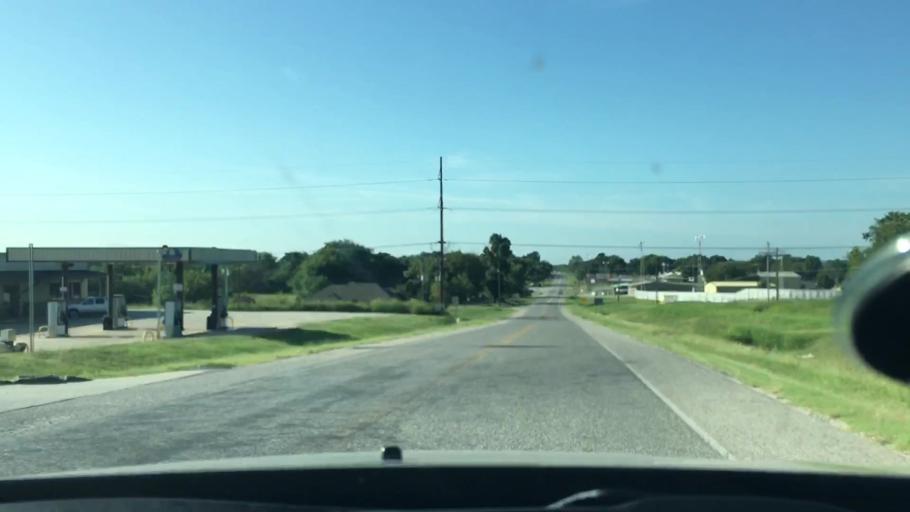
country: US
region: Oklahoma
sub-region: Coal County
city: Coalgate
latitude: 34.6086
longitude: -96.4244
